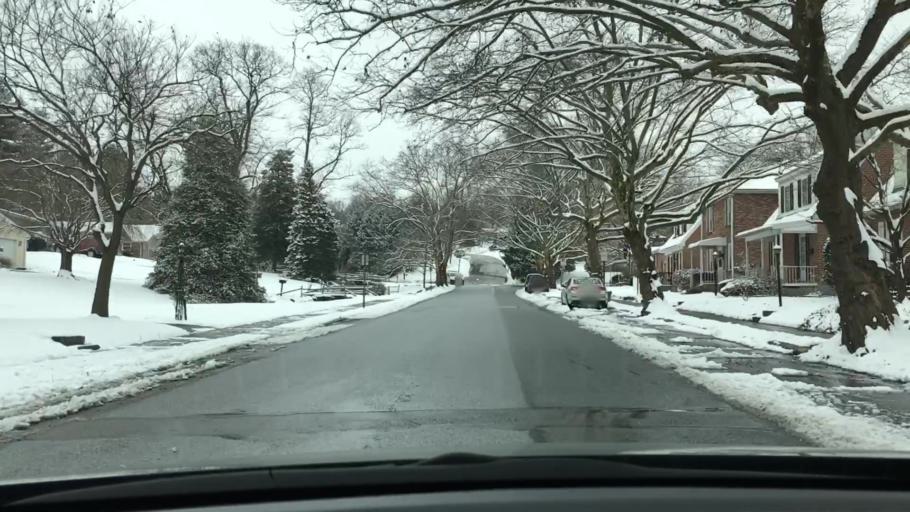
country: US
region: Pennsylvania
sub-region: York County
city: Valley View
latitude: 39.9565
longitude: -76.6975
